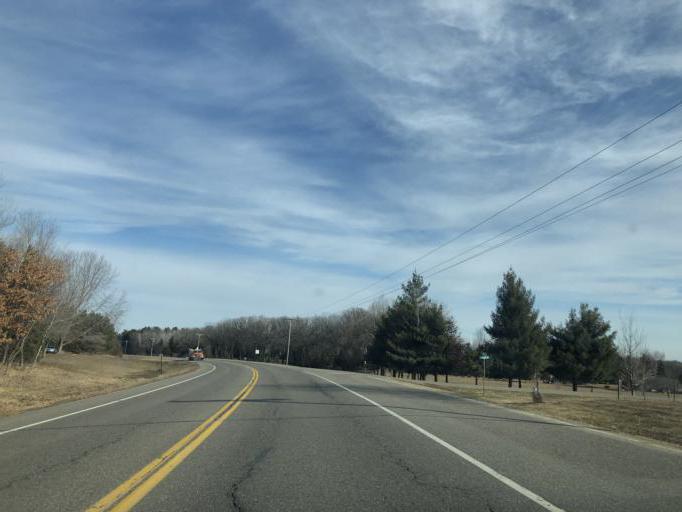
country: US
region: Minnesota
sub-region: Sherburne County
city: Becker
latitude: 45.4191
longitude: -93.8709
